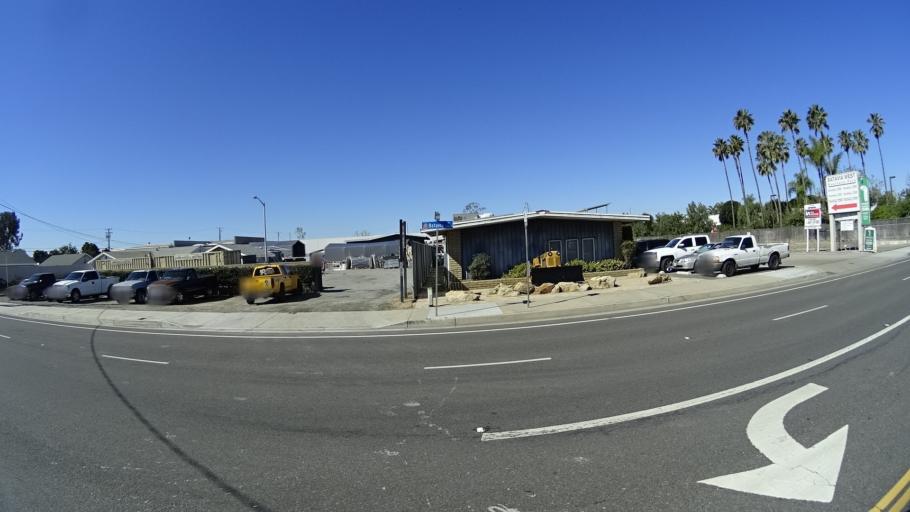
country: US
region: California
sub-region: Orange County
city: Orange
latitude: 33.8261
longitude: -117.8620
